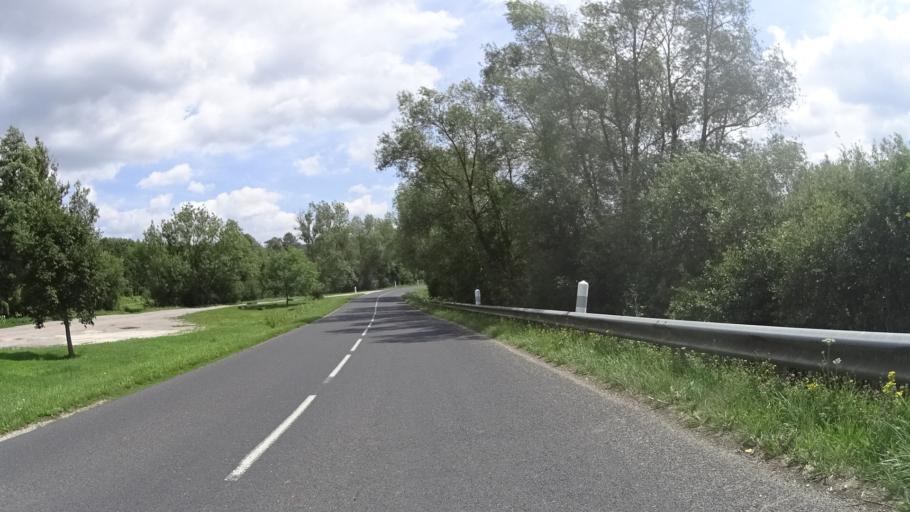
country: FR
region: Lorraine
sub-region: Departement de la Meuse
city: Euville
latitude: 48.7339
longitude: 5.6616
